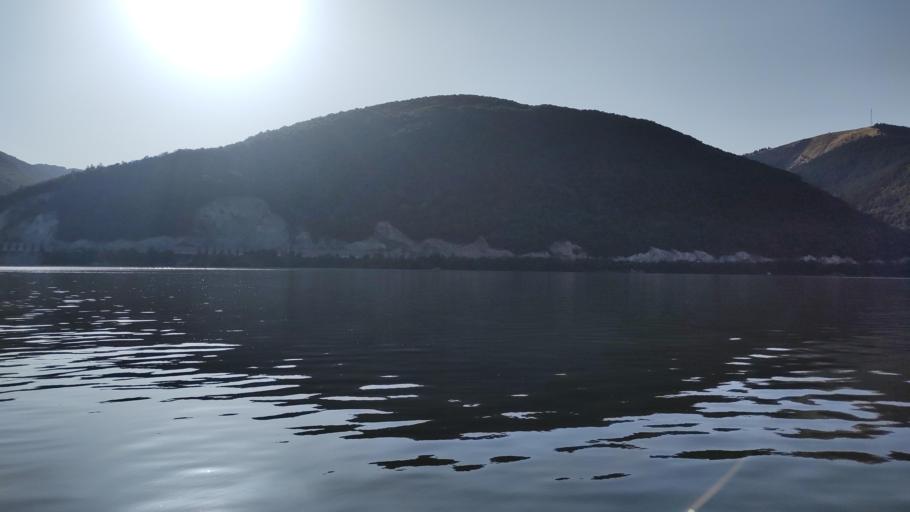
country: RO
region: Mehedinti
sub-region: Comuna Dubova
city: Dubova
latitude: 44.5446
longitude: 22.2222
